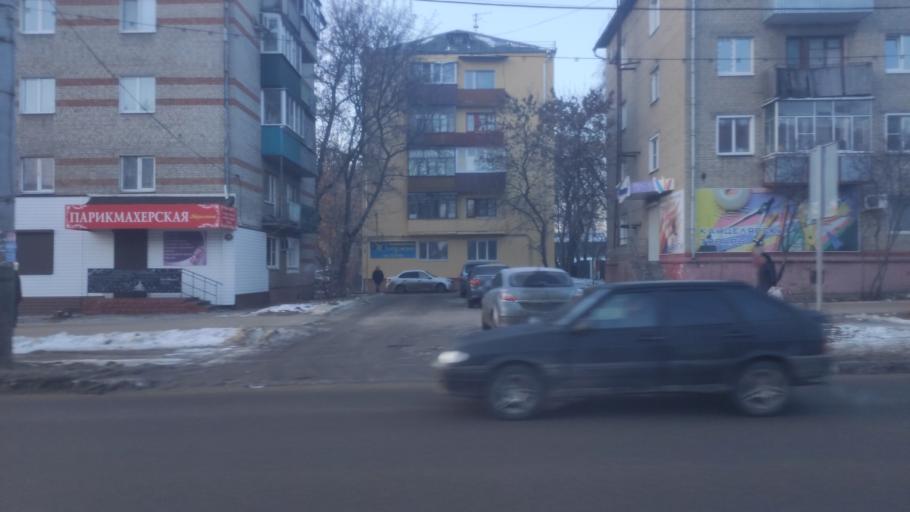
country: RU
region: Tambov
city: Tambov
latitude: 52.7409
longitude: 41.4323
